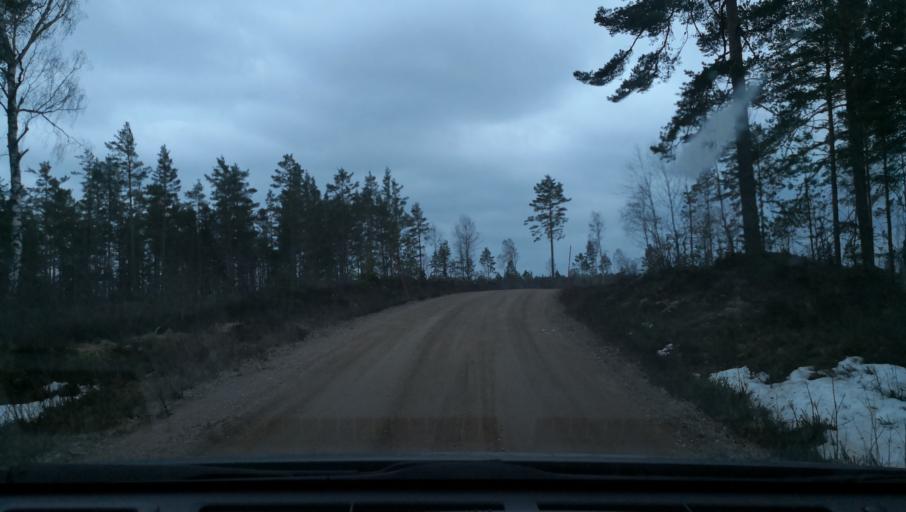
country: SE
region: OErebro
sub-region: Lindesbergs Kommun
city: Fellingsbro
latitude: 59.6028
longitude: 15.5790
